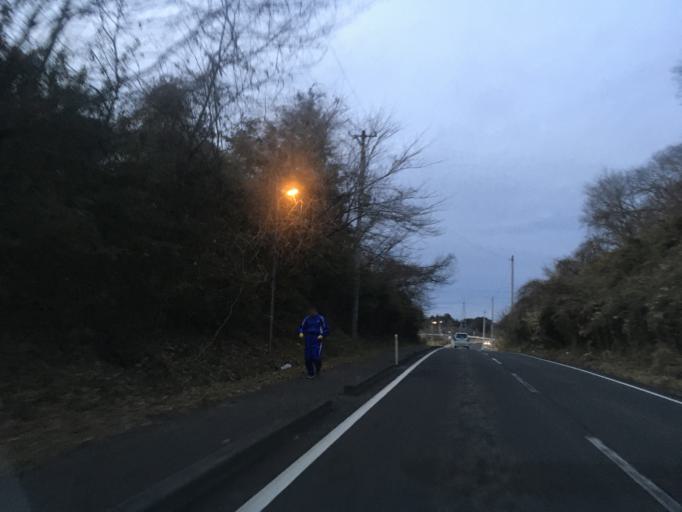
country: JP
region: Miyagi
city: Kogota
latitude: 38.6644
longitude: 141.0723
